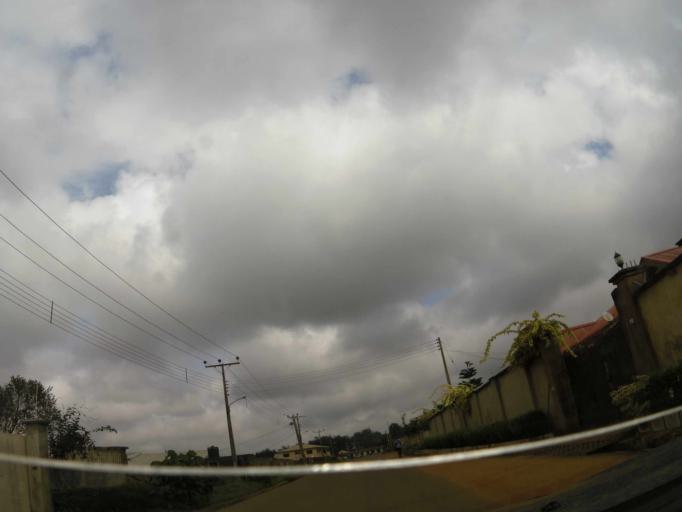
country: NG
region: Oyo
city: Ibadan
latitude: 7.4376
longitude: 3.9534
